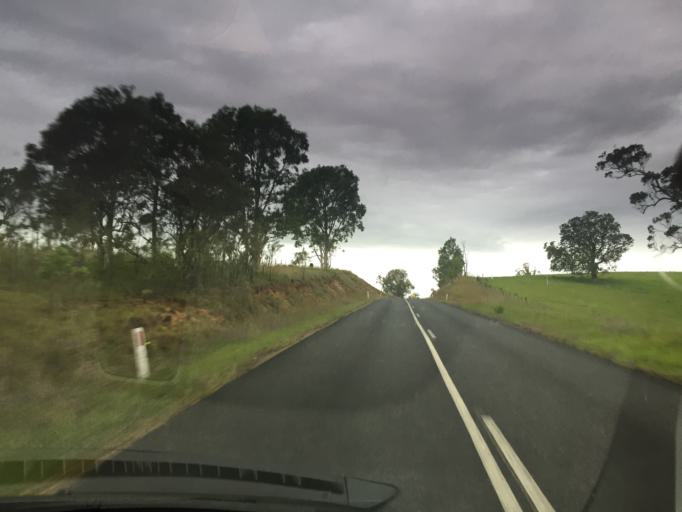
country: AU
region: New South Wales
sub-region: Bega Valley
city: Bega
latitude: -36.6572
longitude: 149.5831
